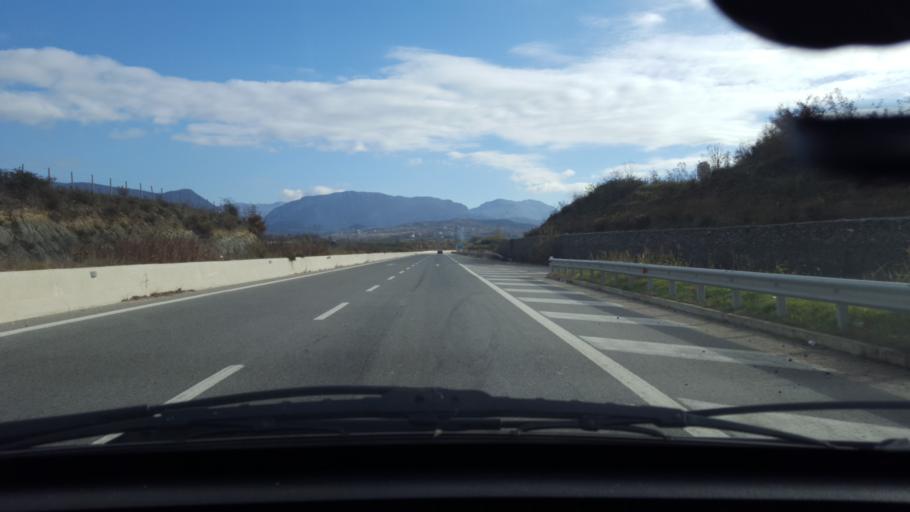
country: AL
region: Tirane
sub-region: Rrethi i Tiranes
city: Berzhite
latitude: 41.2619
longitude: 19.8809
